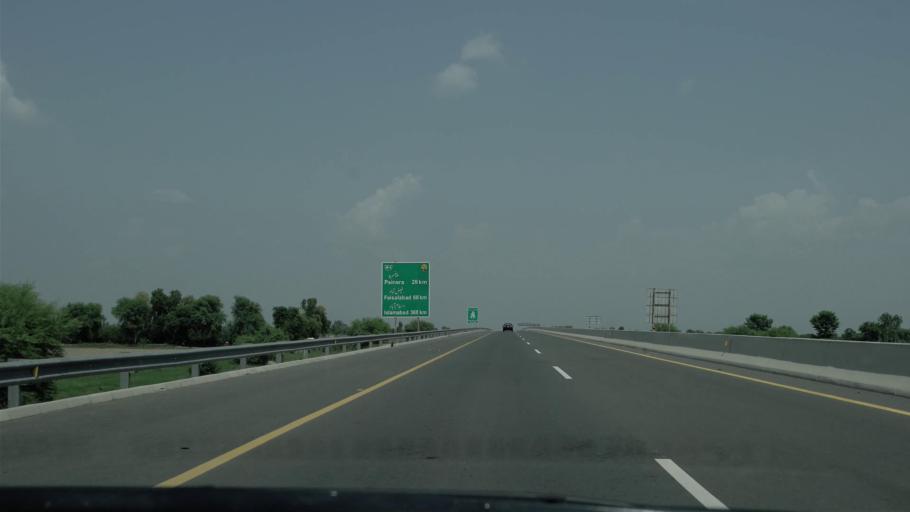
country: PK
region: Punjab
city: Gojra
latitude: 31.1875
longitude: 72.6455
